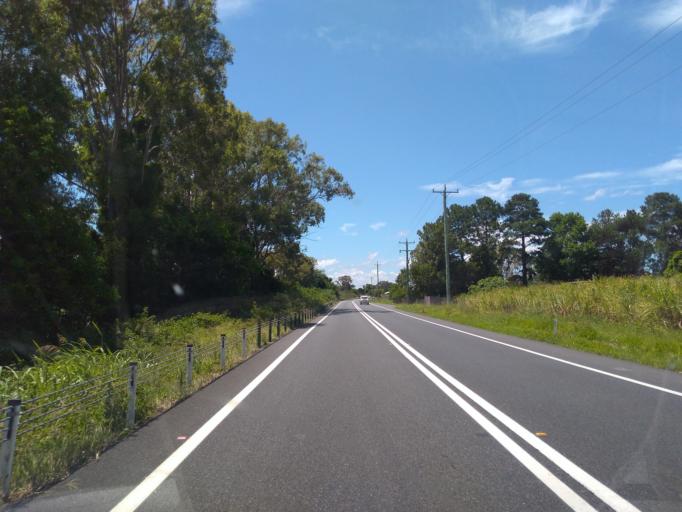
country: AU
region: New South Wales
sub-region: Clarence Valley
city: Maclean
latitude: -29.5235
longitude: 153.1859
